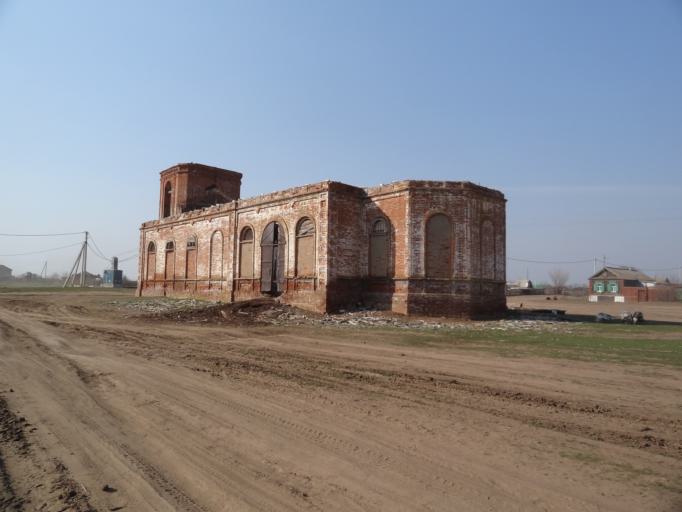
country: RU
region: Saratov
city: Privolzhskiy
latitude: 51.3246
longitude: 45.9773
